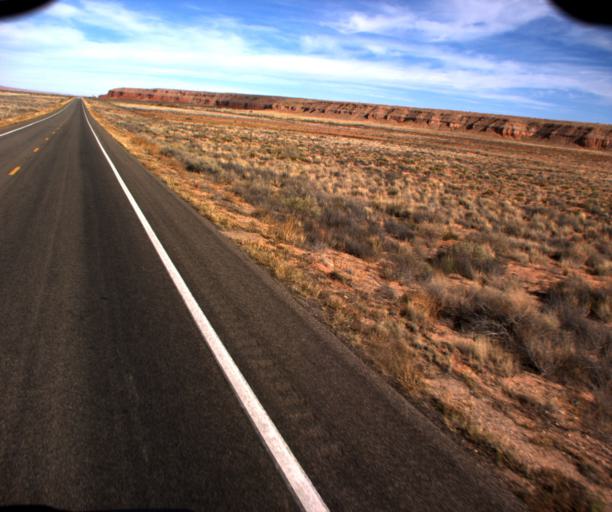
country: US
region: Arizona
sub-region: Navajo County
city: Kayenta
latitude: 36.7505
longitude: -110.0623
